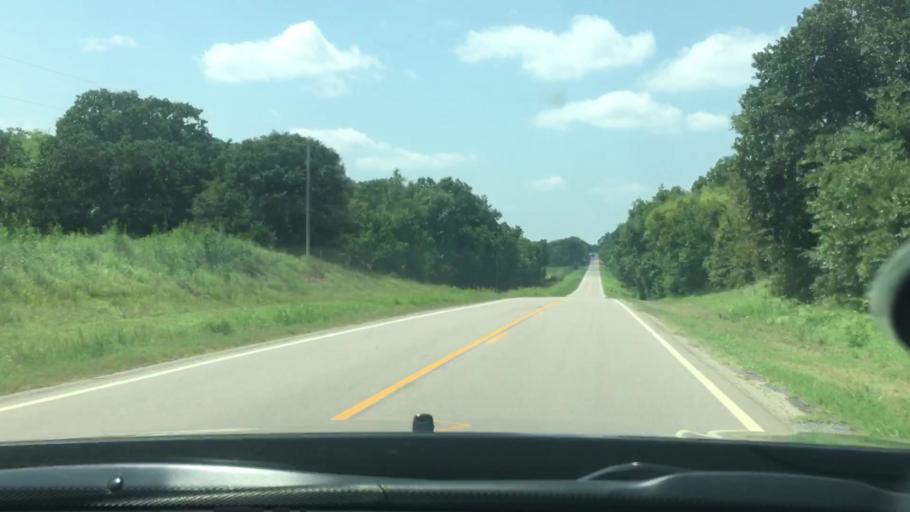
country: US
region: Oklahoma
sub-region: Coal County
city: Coalgate
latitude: 34.3701
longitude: -96.3471
